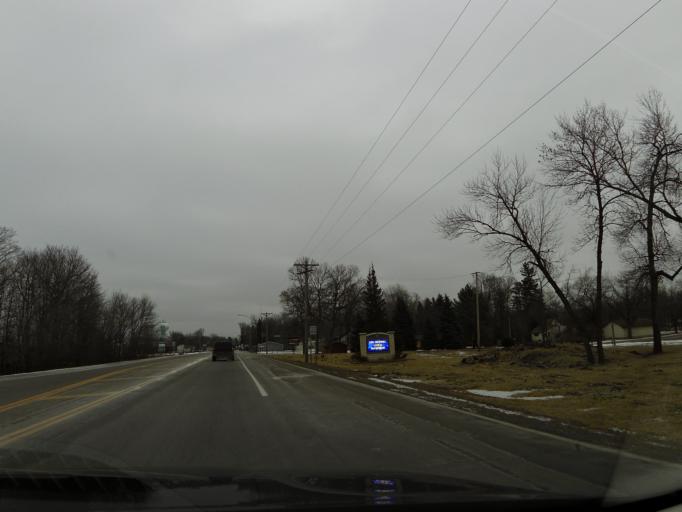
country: US
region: Minnesota
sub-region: Hennepin County
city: Maple Plain
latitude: 45.0094
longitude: -93.6641
